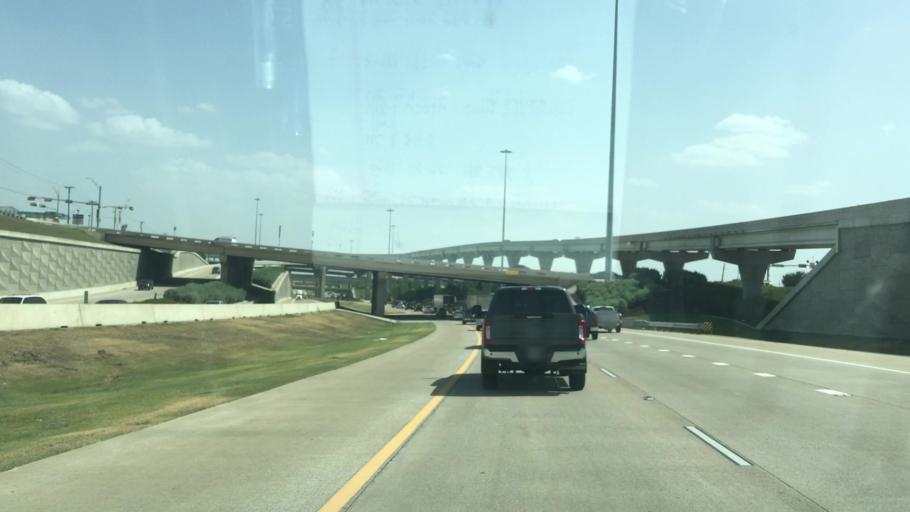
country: US
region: Texas
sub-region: Dallas County
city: Grand Prairie
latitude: 32.7663
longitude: -97.0290
